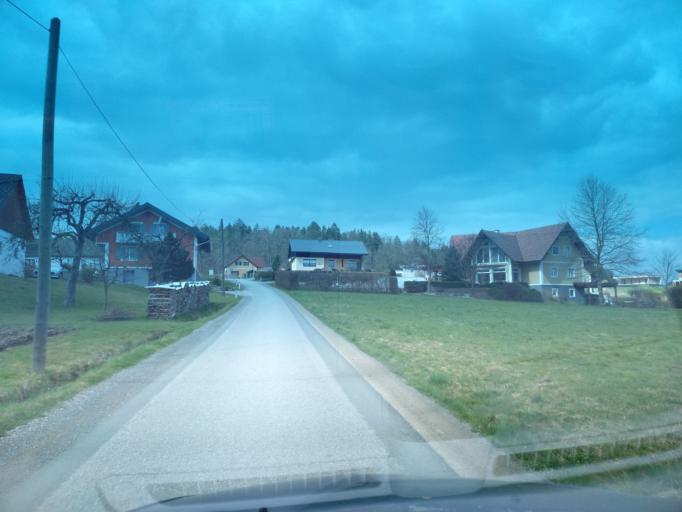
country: AT
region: Styria
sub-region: Politischer Bezirk Leibnitz
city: Grossklein
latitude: 46.7414
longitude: 15.4297
